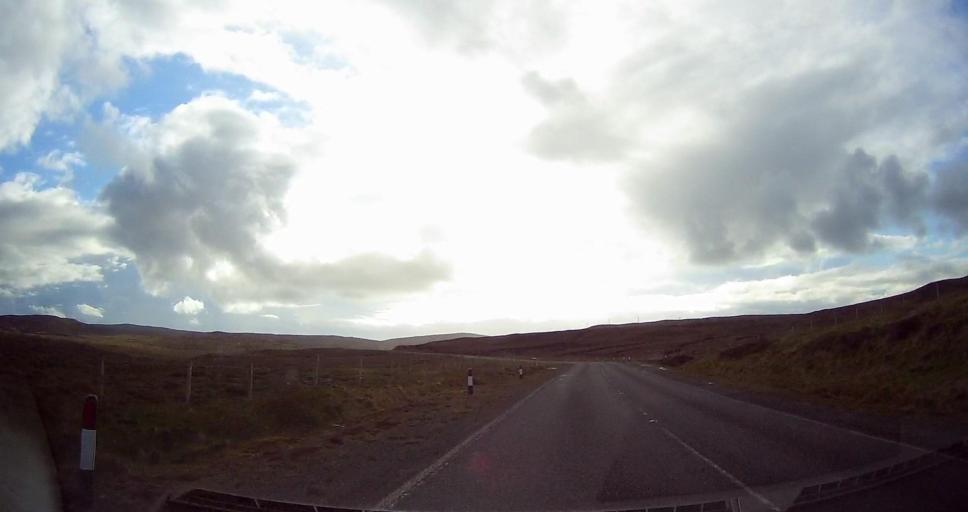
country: GB
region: Scotland
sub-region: Shetland Islands
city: Lerwick
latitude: 60.3491
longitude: -1.2119
